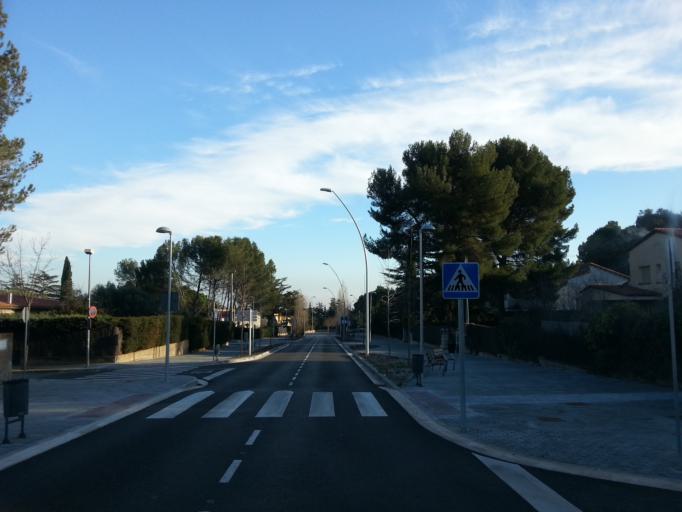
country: ES
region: Catalonia
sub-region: Provincia de Barcelona
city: Matadepera
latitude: 41.6030
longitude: 2.0188
